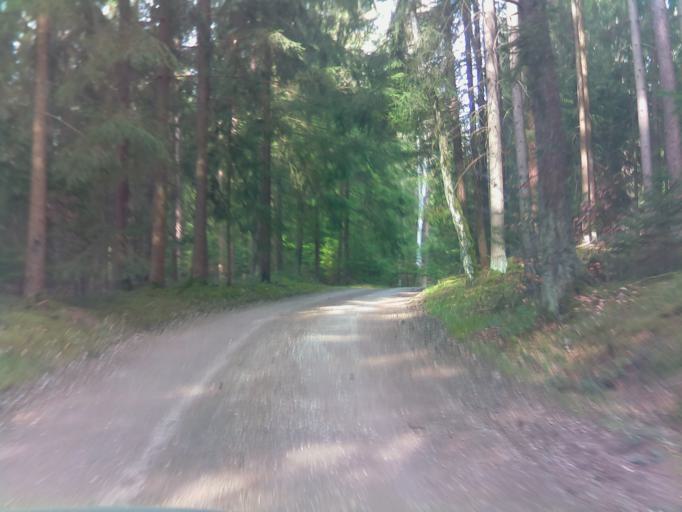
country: DE
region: Bavaria
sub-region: Upper Palatinate
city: Freudenberg
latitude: 49.4698
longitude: 12.0119
